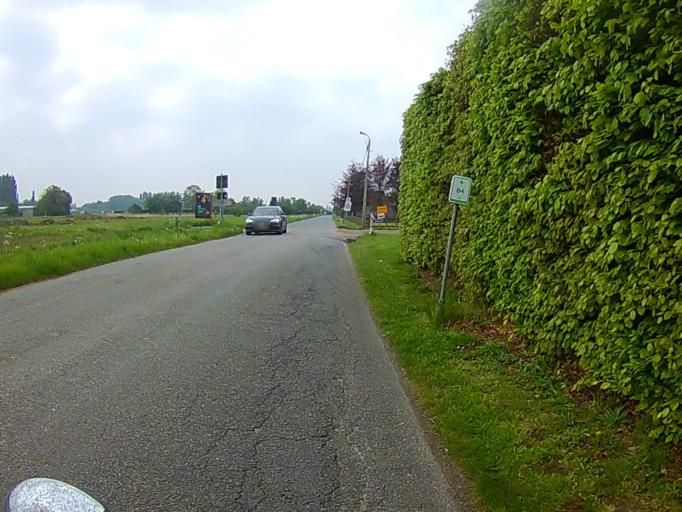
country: BE
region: Flanders
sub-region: Provincie Antwerpen
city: Wommelgem
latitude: 51.1908
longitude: 4.5265
